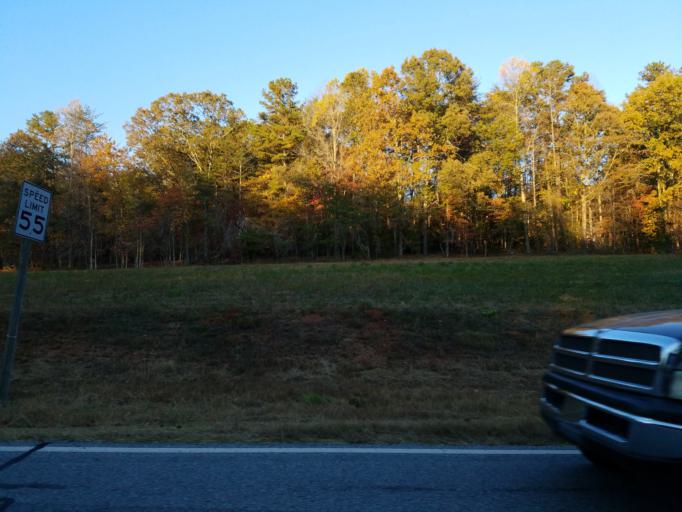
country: US
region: Georgia
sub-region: Lumpkin County
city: Dahlonega
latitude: 34.5205
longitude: -84.0459
